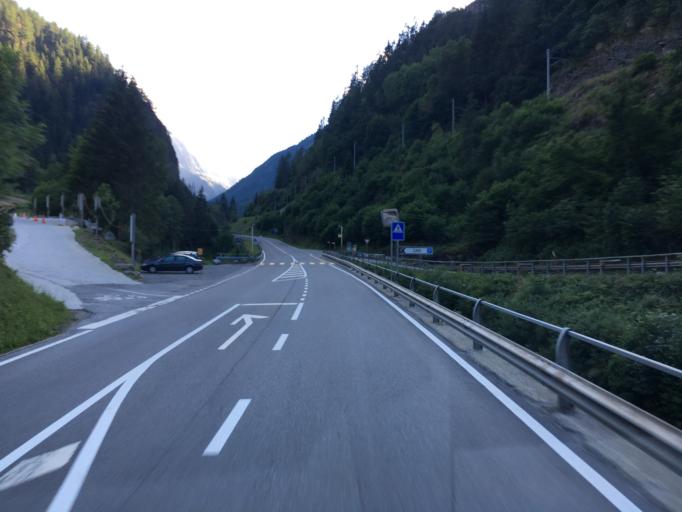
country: CH
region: Valais
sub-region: Saint-Maurice District
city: Salvan
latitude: 46.0588
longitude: 6.9593
